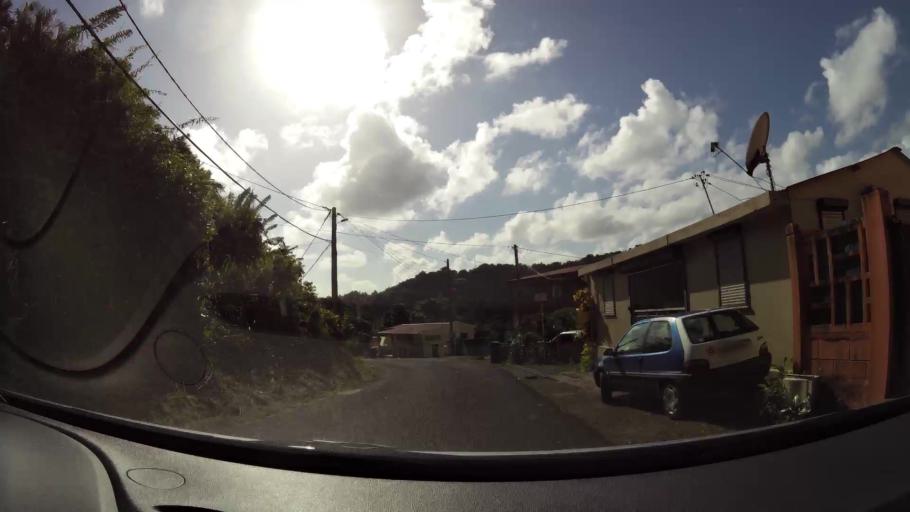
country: MQ
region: Martinique
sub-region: Martinique
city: La Trinite
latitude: 14.7378
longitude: -60.9678
